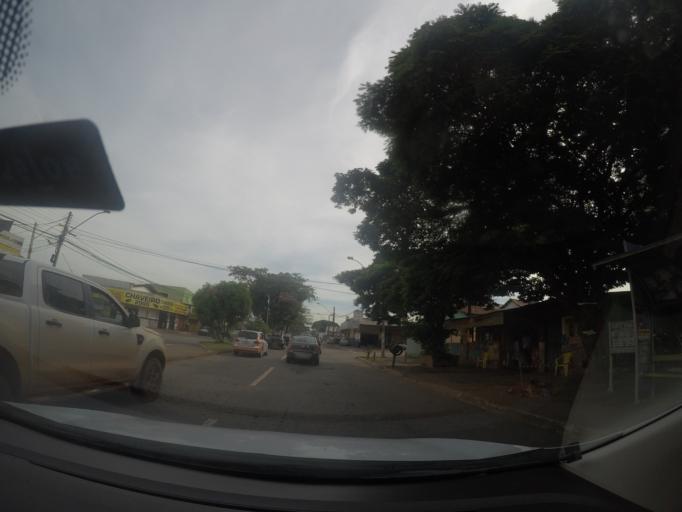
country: BR
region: Goias
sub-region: Goiania
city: Goiania
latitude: -16.6706
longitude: -49.3137
